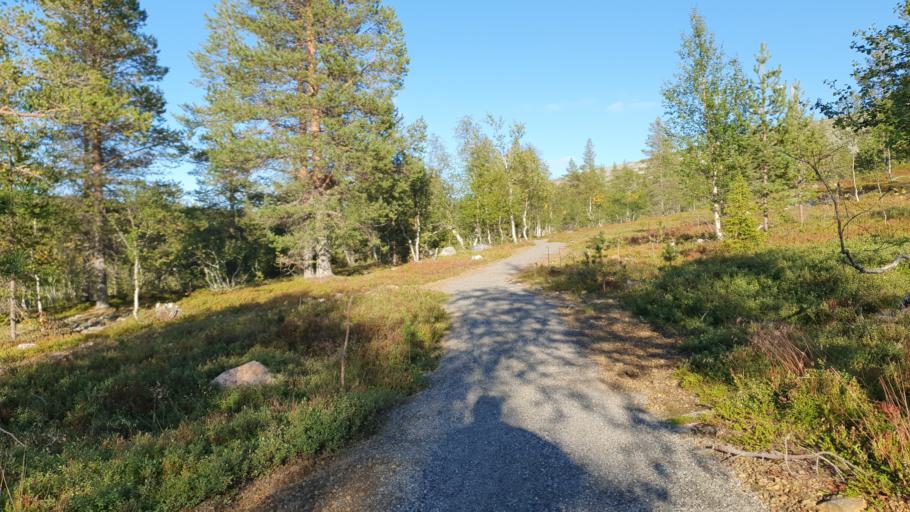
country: FI
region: Lapland
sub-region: Tunturi-Lappi
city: Kolari
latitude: 67.5822
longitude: 24.2203
